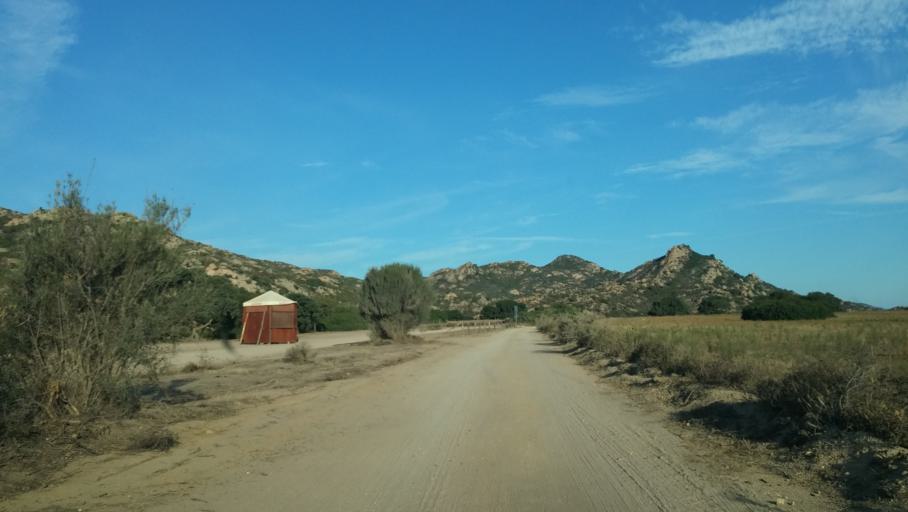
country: IT
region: Sardinia
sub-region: Provincia di Nuoro
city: La Caletta
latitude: 40.4811
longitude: 9.8065
